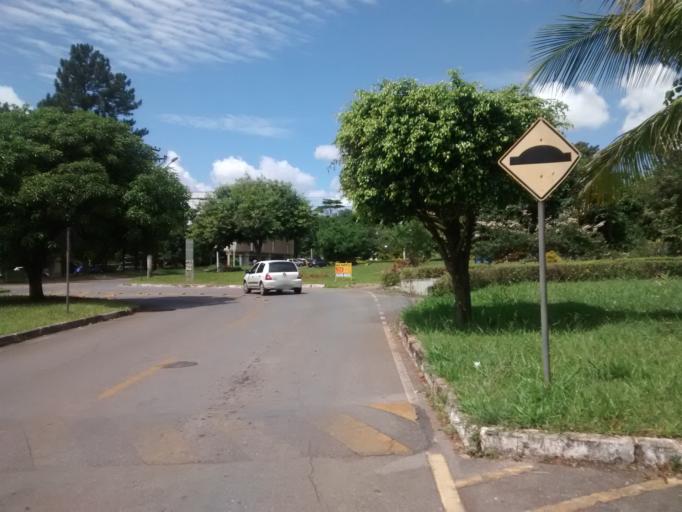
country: BR
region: Federal District
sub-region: Brasilia
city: Brasilia
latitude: -15.7565
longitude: -47.8752
